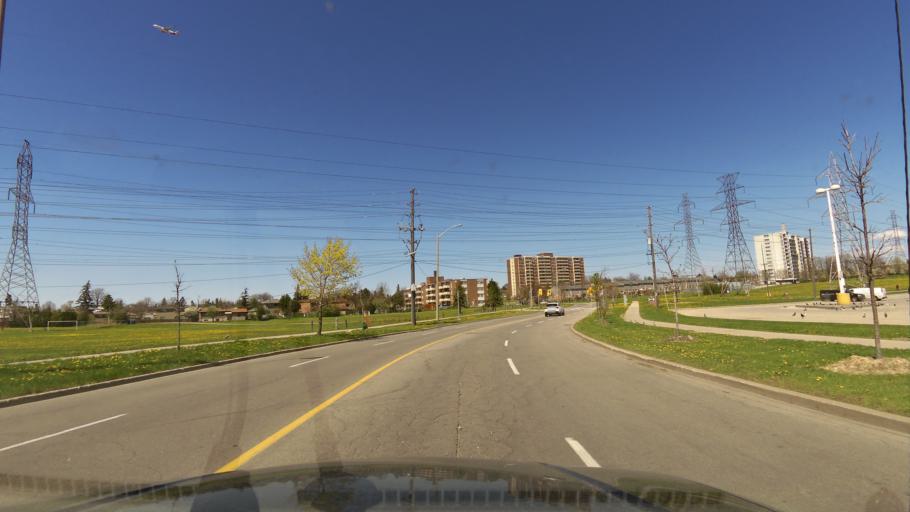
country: CA
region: Ontario
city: Concord
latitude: 43.7589
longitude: -79.5216
